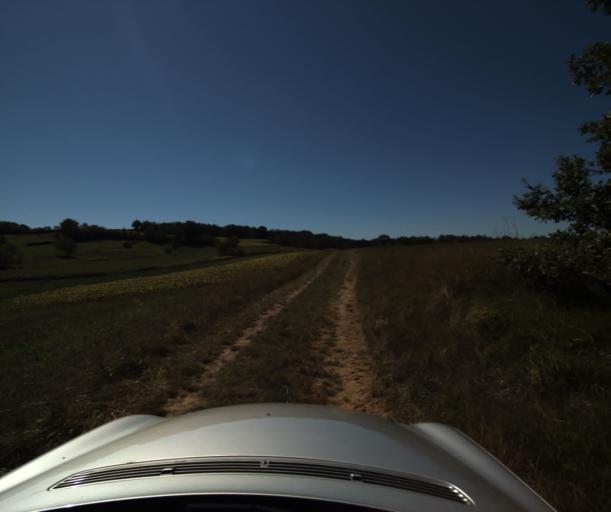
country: FR
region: Midi-Pyrenees
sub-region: Departement de l'Ariege
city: Belesta
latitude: 42.9681
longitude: 1.9282
